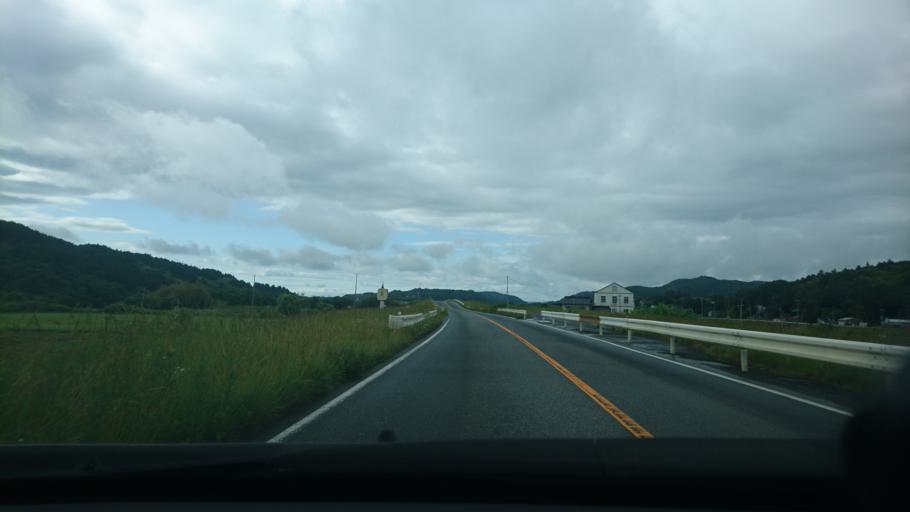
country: JP
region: Miyagi
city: Wakuya
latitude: 38.6382
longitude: 141.2886
